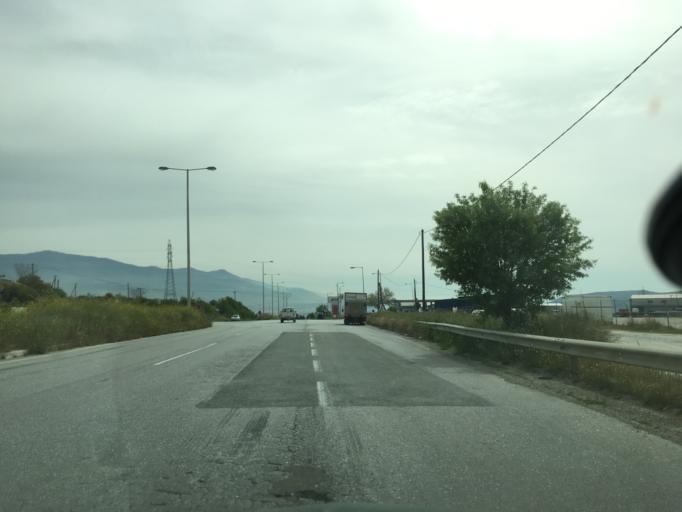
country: GR
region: Thessaly
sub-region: Nomos Magnisias
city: Nea Ionia
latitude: 39.3804
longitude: 22.8657
